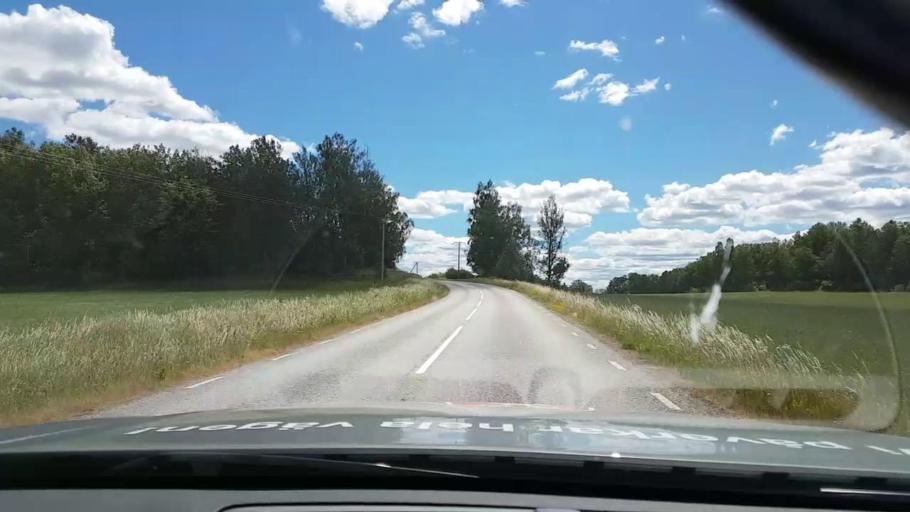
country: SE
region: Kalmar
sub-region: Vasterviks Kommun
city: Overum
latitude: 58.0518
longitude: 16.4060
